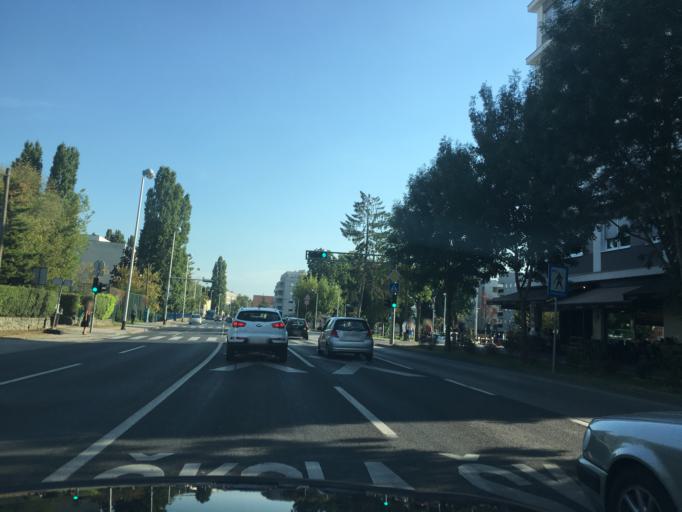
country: HR
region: Grad Zagreb
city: Zagreb - Centar
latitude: 45.8036
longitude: 15.9430
